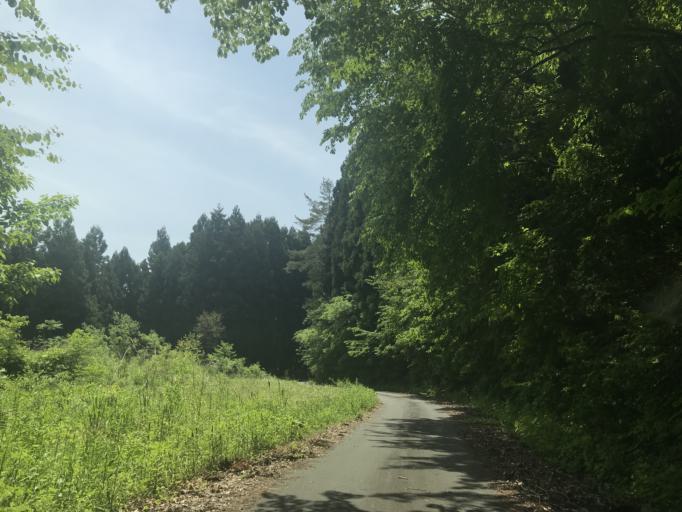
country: JP
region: Iwate
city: Ichinoseki
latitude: 38.9520
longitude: 141.2456
